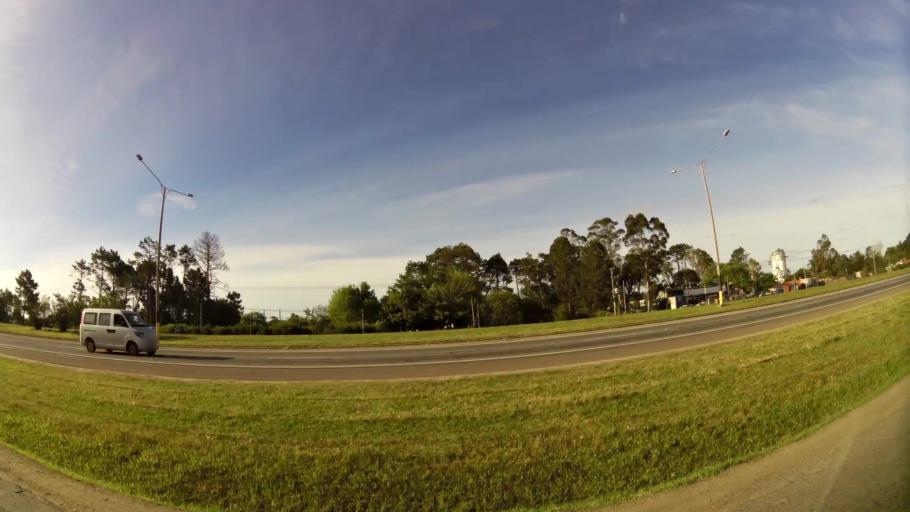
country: UY
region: Canelones
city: Empalme Olmos
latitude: -34.7784
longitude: -55.8595
